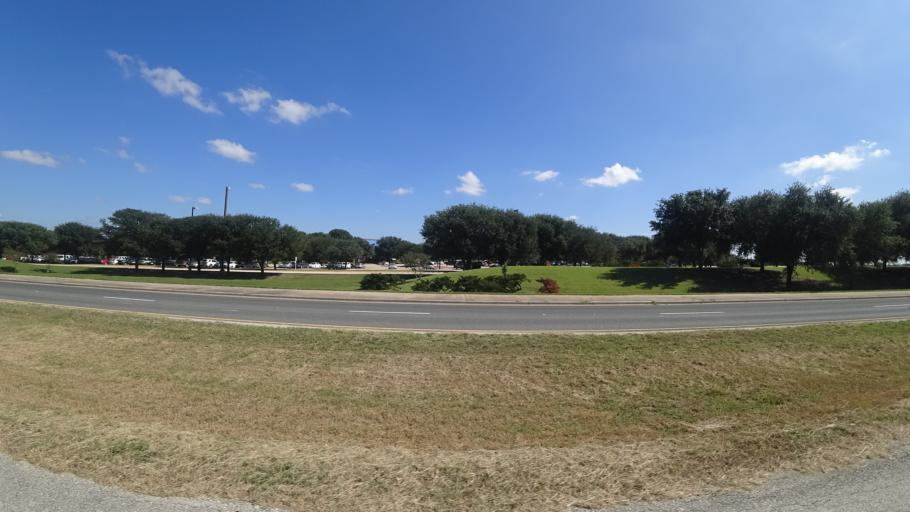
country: US
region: Texas
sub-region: Travis County
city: Manor
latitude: 30.3373
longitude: -97.6197
